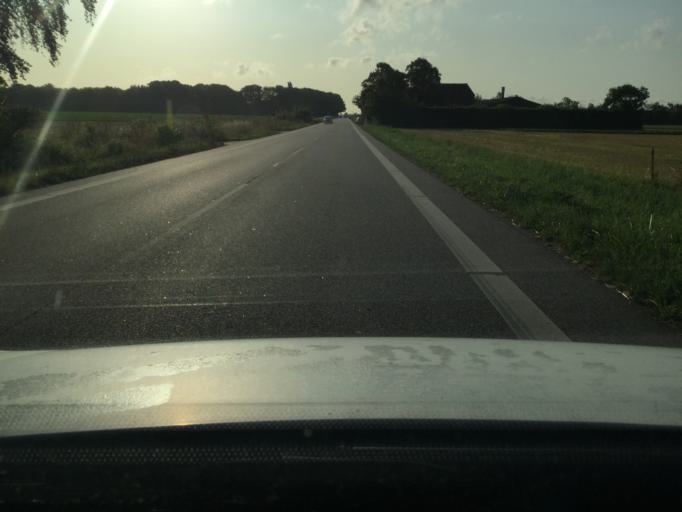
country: DK
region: Zealand
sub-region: Lolland Kommune
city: Rodby
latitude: 54.7572
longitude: 11.3432
